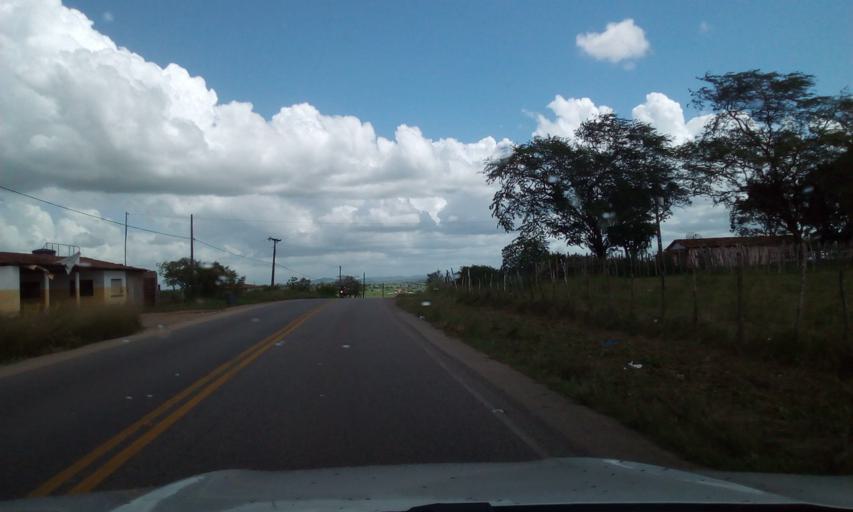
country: BR
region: Paraiba
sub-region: Guarabira
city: Guarabira
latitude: -6.8464
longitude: -35.3604
